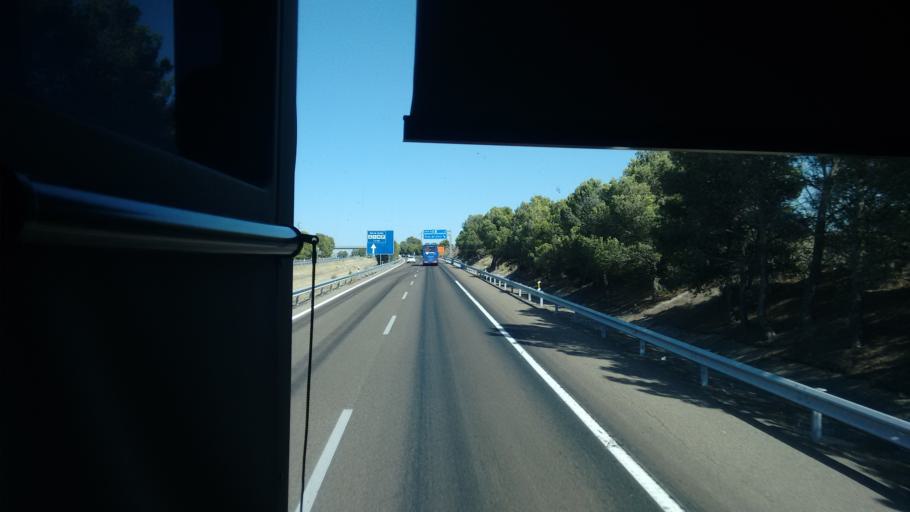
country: ES
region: Aragon
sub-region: Provincia de Zaragoza
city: Pina de Ebro
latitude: 41.5236
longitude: -0.4696
